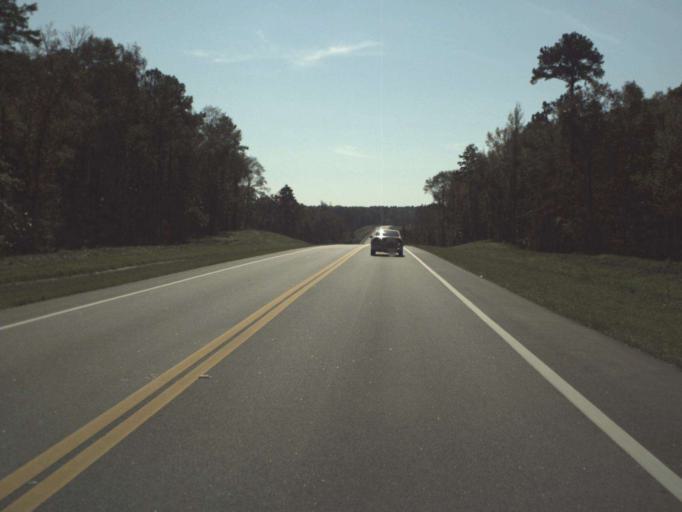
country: US
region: Florida
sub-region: Gadsden County
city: Quincy
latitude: 30.5896
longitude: -84.5534
